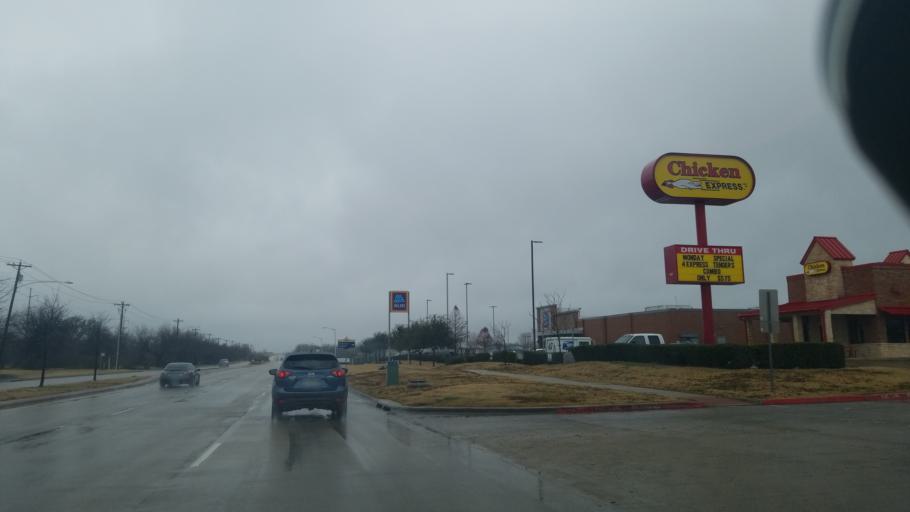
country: US
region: Texas
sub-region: Denton County
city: Denton
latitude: 33.1994
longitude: -97.0911
